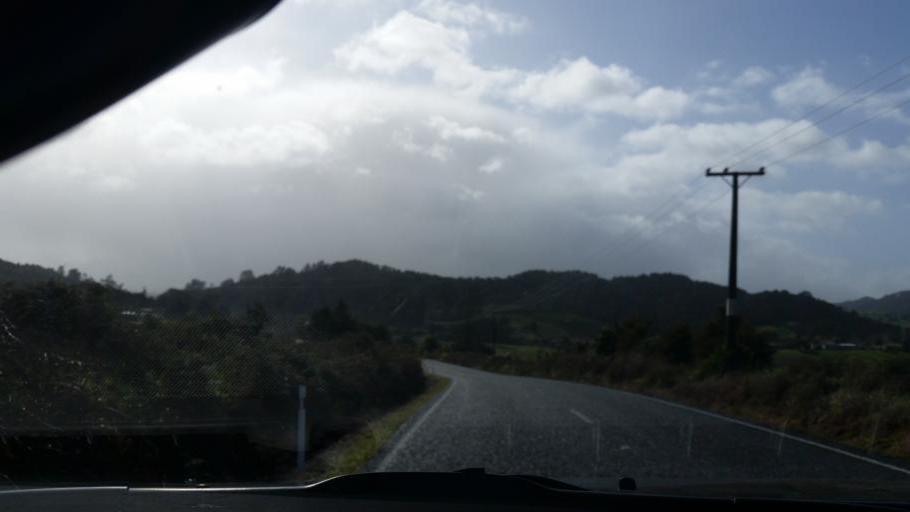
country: NZ
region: Northland
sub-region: Whangarei
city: Ruakaka
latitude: -36.0441
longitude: 174.2786
